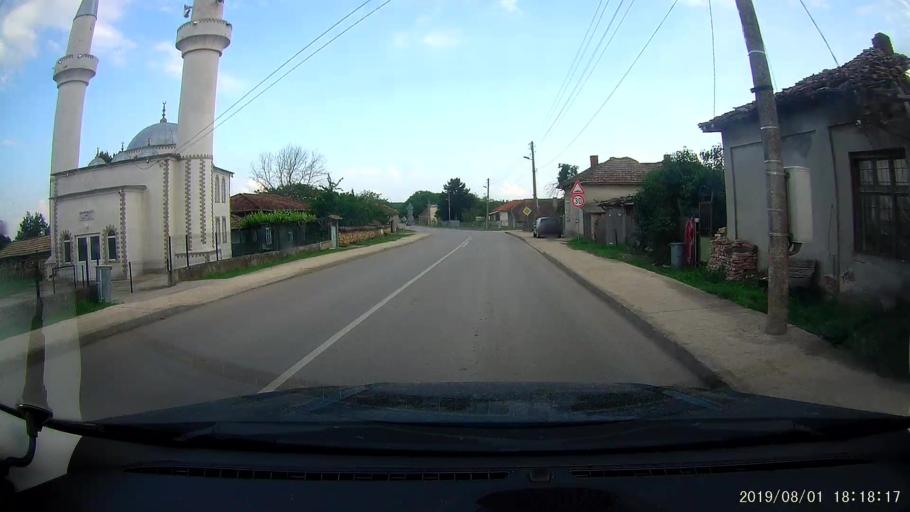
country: BG
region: Shumen
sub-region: Obshtina Kaolinovo
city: Kaolinovo
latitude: 43.6998
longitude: 27.0802
